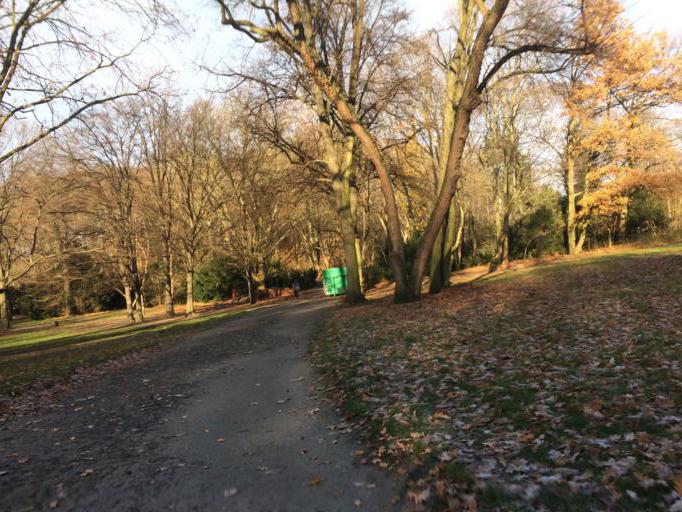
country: DE
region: Berlin
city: Gesundbrunnen
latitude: 52.5455
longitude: 13.3870
